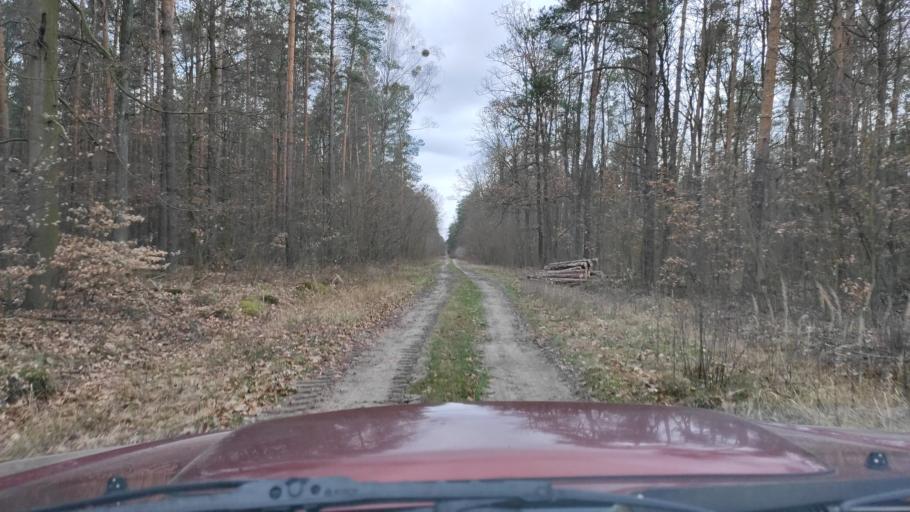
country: PL
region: Masovian Voivodeship
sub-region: Powiat kozienicki
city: Garbatka-Letnisko
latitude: 51.5057
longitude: 21.5569
